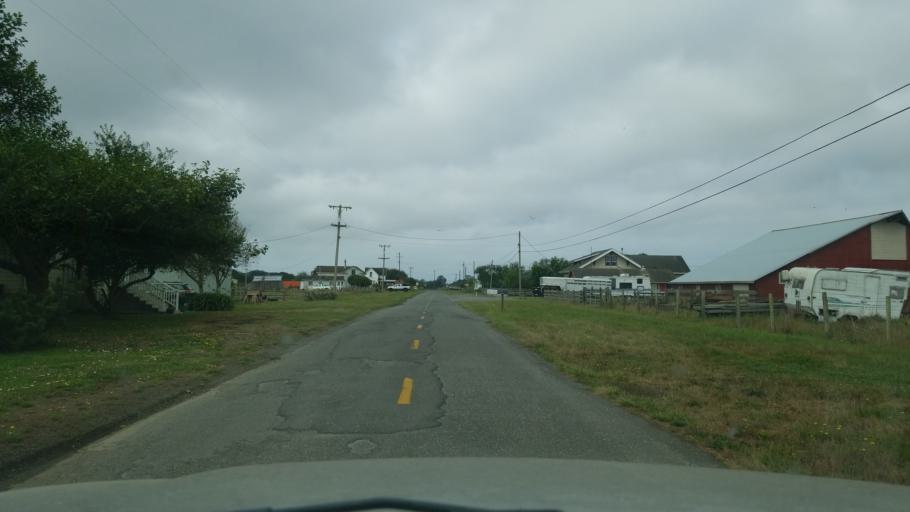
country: US
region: California
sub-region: Humboldt County
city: Ferndale
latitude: 40.5953
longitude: -124.2811
